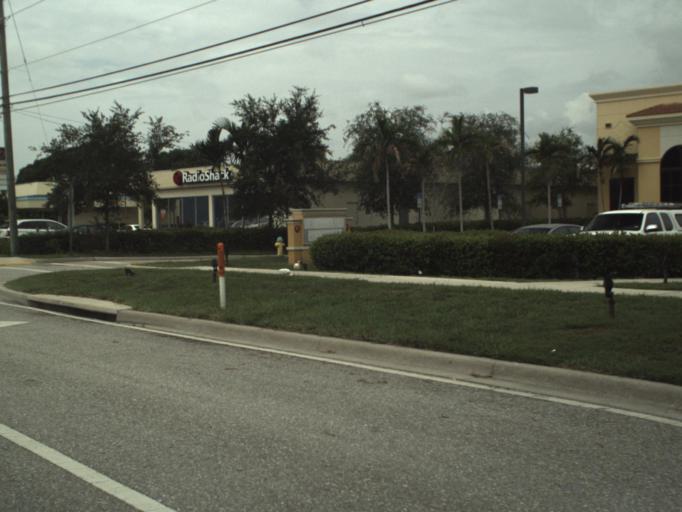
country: US
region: Florida
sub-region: Broward County
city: Deerfield Beach
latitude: 26.3095
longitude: -80.0923
